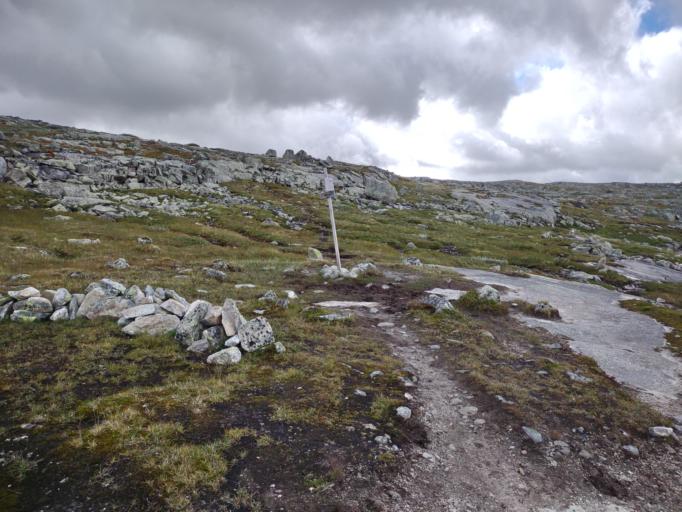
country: NO
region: Hordaland
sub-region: Eidfjord
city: Eidfjord
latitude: 60.5600
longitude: 7.5368
